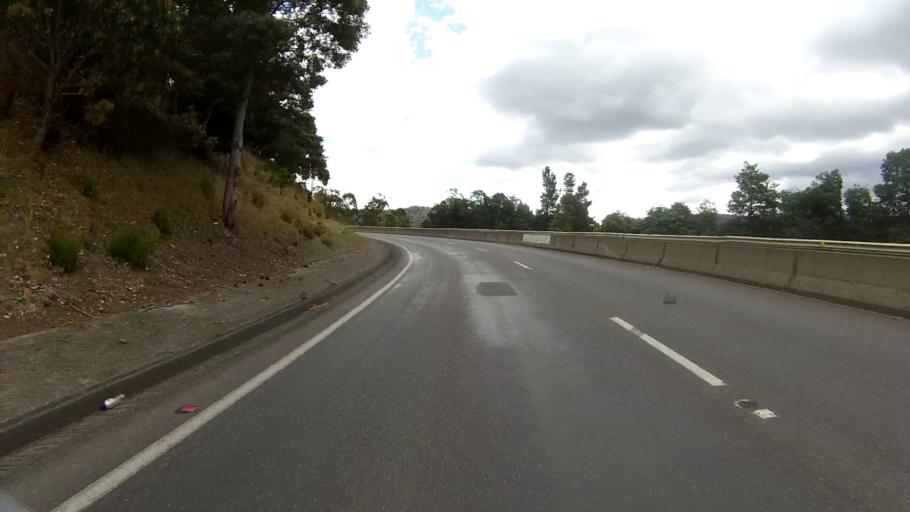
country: AU
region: Tasmania
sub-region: Kingborough
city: Margate
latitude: -42.9798
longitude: 147.1720
